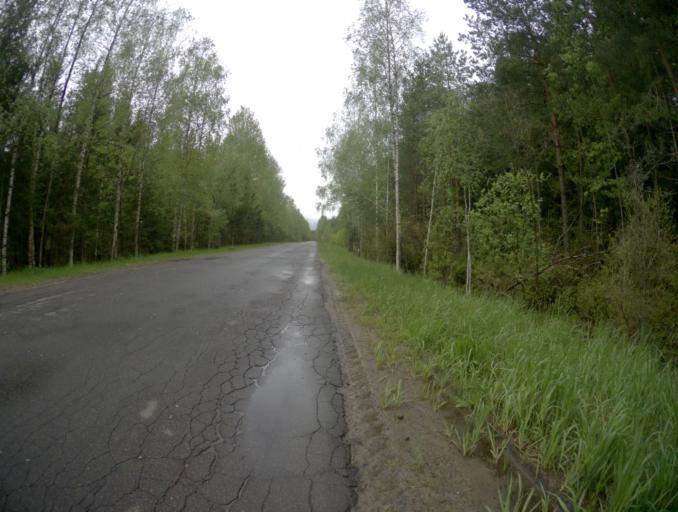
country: RU
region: Vladimir
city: Zolotkovo
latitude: 55.3466
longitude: 40.9699
